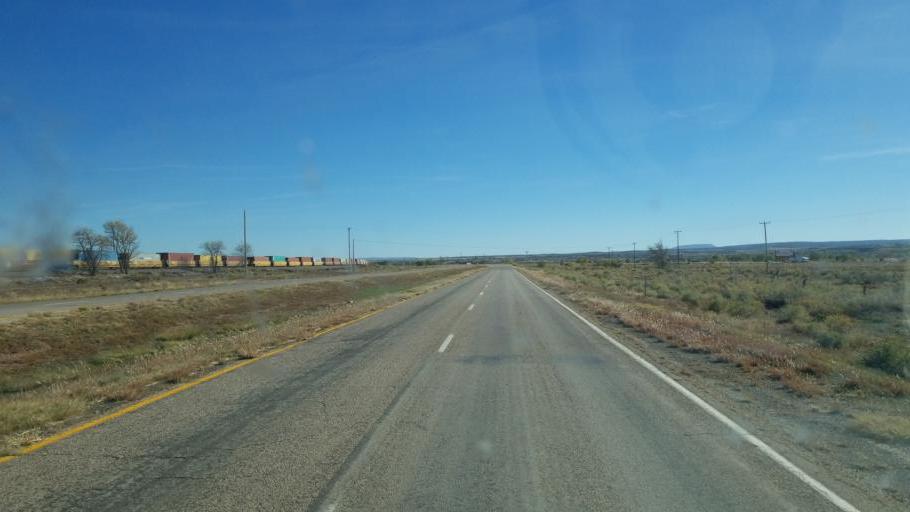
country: US
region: New Mexico
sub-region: Cibola County
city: Milan
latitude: 35.2735
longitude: -107.9799
